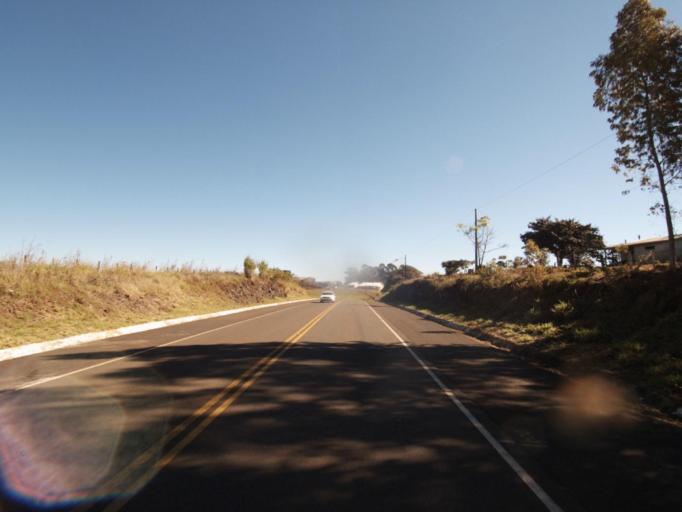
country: AR
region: Misiones
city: Bernardo de Irigoyen
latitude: -26.6698
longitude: -53.5962
